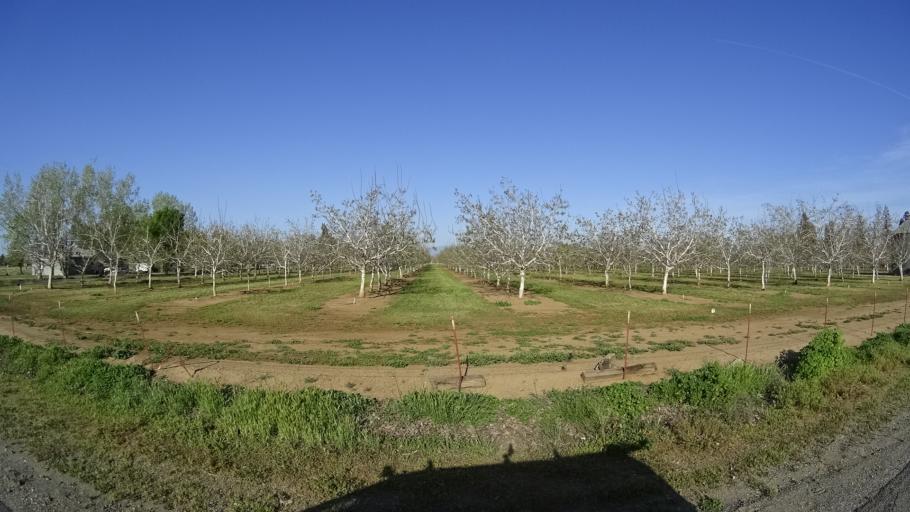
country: US
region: California
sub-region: Glenn County
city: Willows
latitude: 39.5172
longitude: -122.2267
